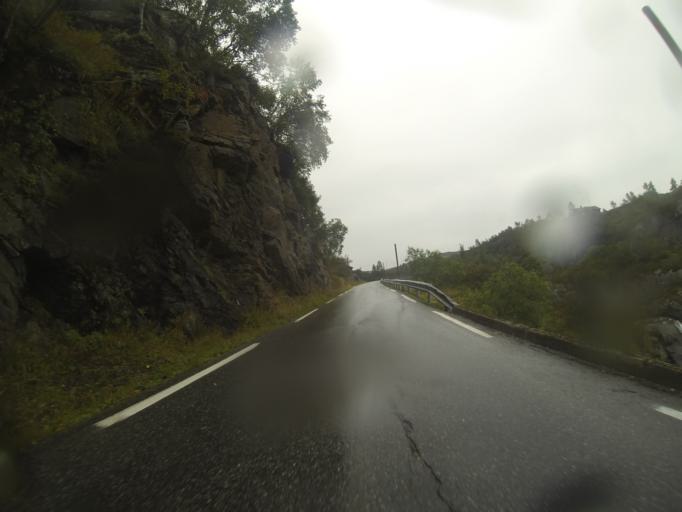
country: NO
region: Rogaland
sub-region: Sauda
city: Sauda
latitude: 59.7250
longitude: 6.5714
